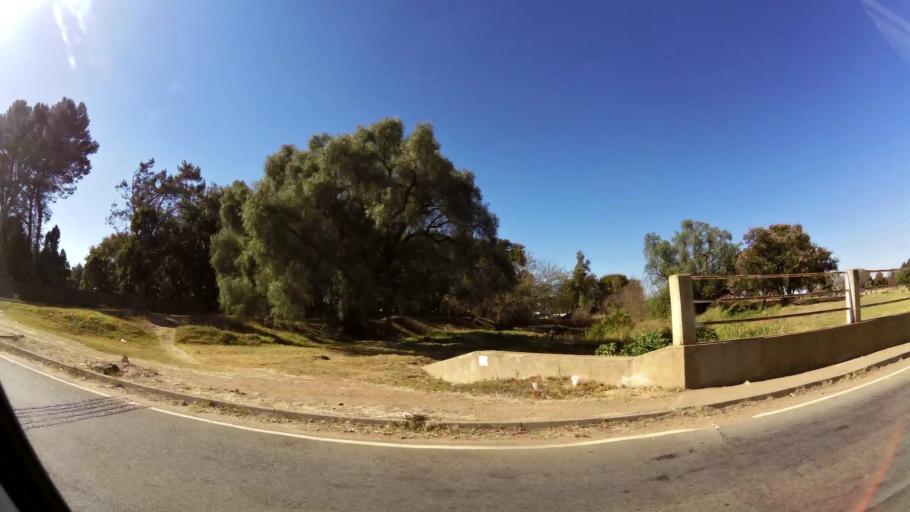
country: ZA
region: Limpopo
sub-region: Capricorn District Municipality
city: Polokwane
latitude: -23.9111
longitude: 29.4450
